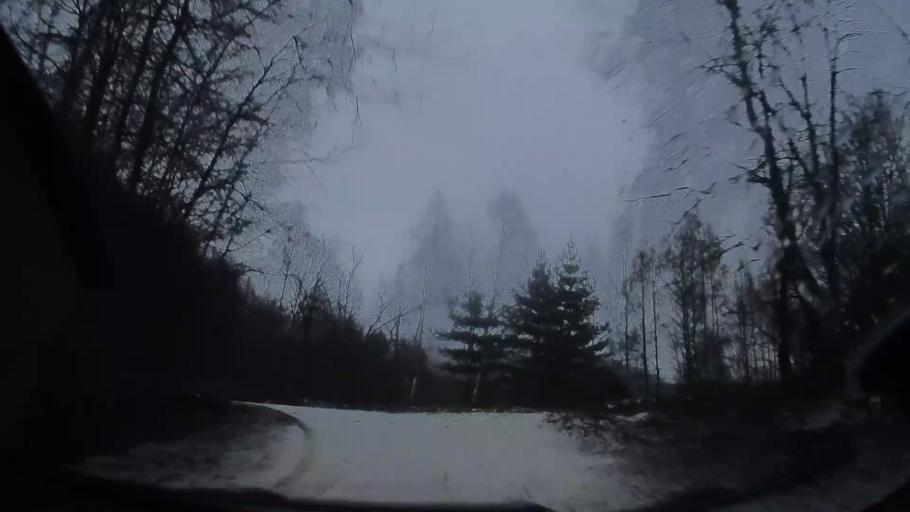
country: RO
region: Alba
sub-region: Comuna Avram Iancu
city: Avram Iancu
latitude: 46.3045
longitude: 22.7961
